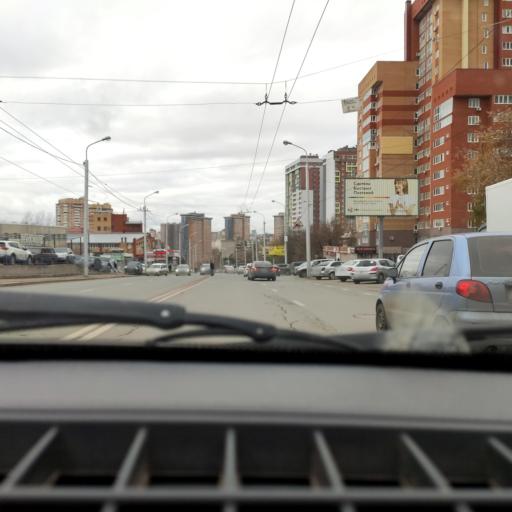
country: RU
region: Bashkortostan
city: Ufa
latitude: 54.7145
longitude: 55.9957
